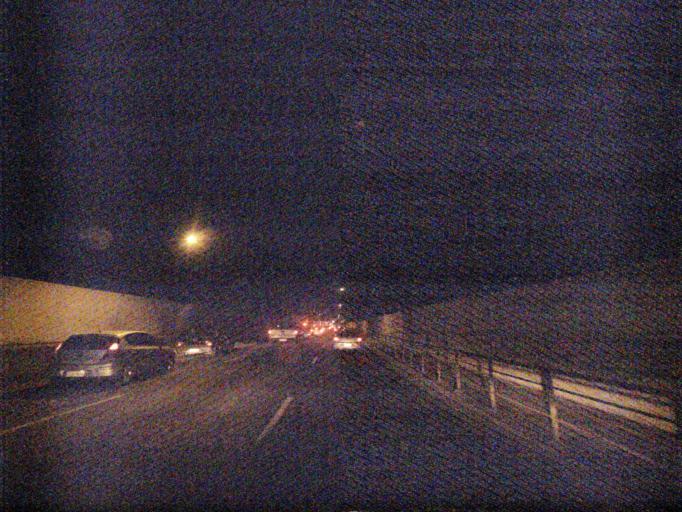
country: BR
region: Rio de Janeiro
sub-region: Niteroi
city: Niteroi
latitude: -22.9128
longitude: -43.0974
